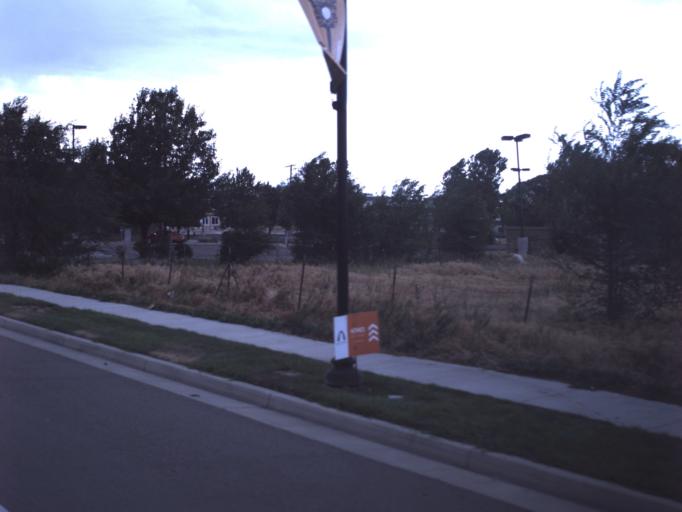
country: US
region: Utah
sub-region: Salt Lake County
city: Riverton
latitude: 40.5224
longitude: -111.9275
